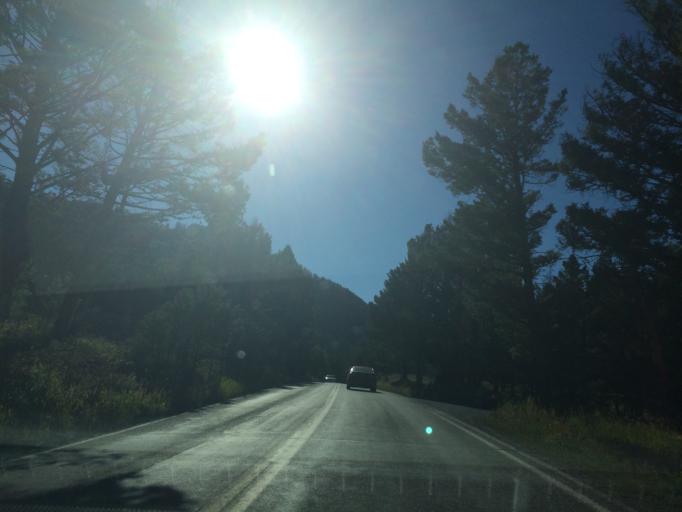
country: US
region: Montana
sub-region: Gallatin County
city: West Yellowstone
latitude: 44.9475
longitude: -110.4531
